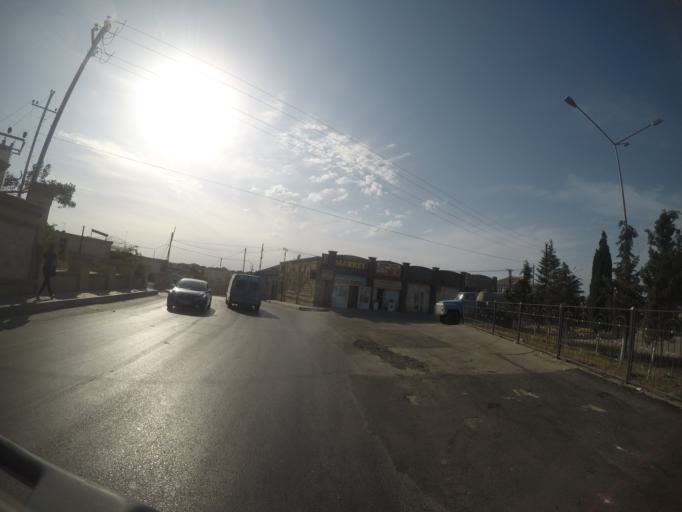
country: AZ
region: Baki
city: Binagadi
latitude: 40.4685
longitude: 49.8415
